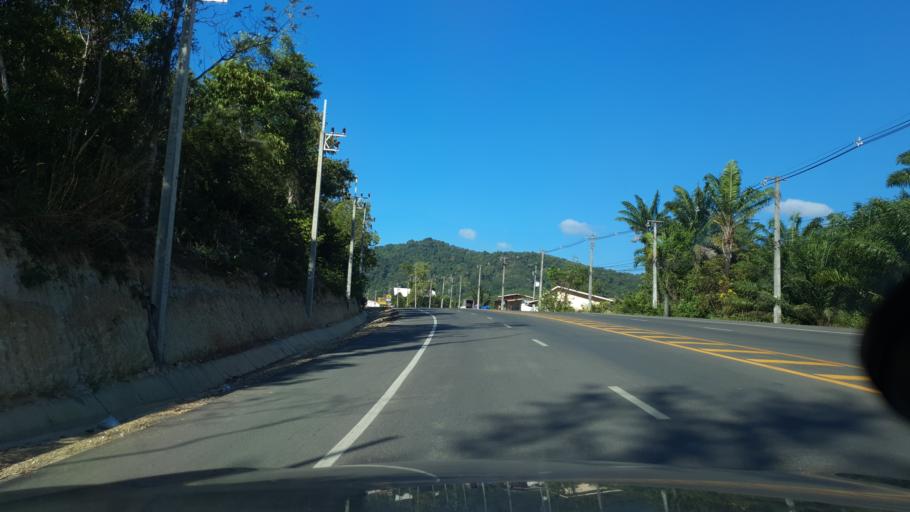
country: TH
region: Phangnga
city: Ban Ao Nang
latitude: 8.0421
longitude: 98.8471
